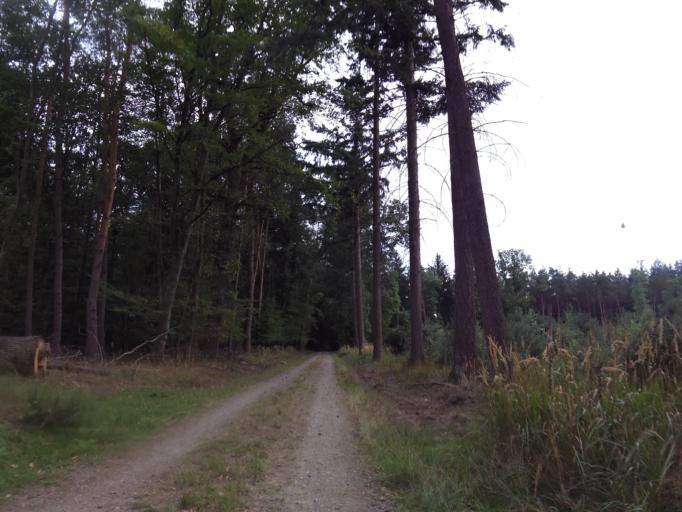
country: DE
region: Hesse
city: Morfelden-Walldorf
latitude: 50.0132
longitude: 8.5467
